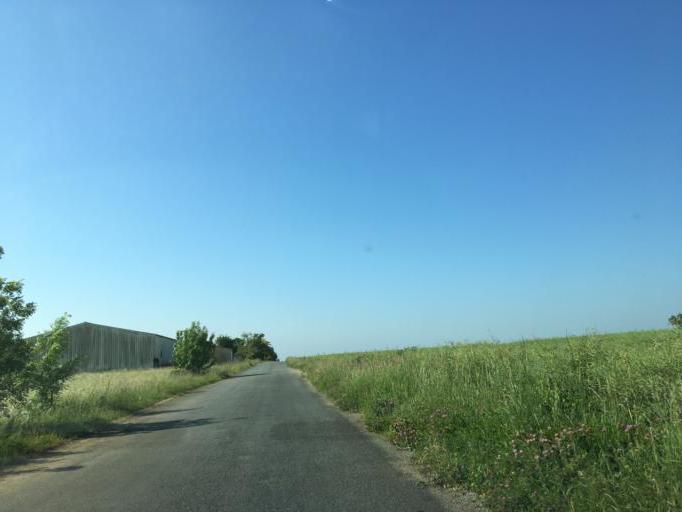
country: FR
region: Poitou-Charentes
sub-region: Departement des Deux-Sevres
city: Beauvoir-sur-Niort
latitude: 46.0859
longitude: -0.5068
